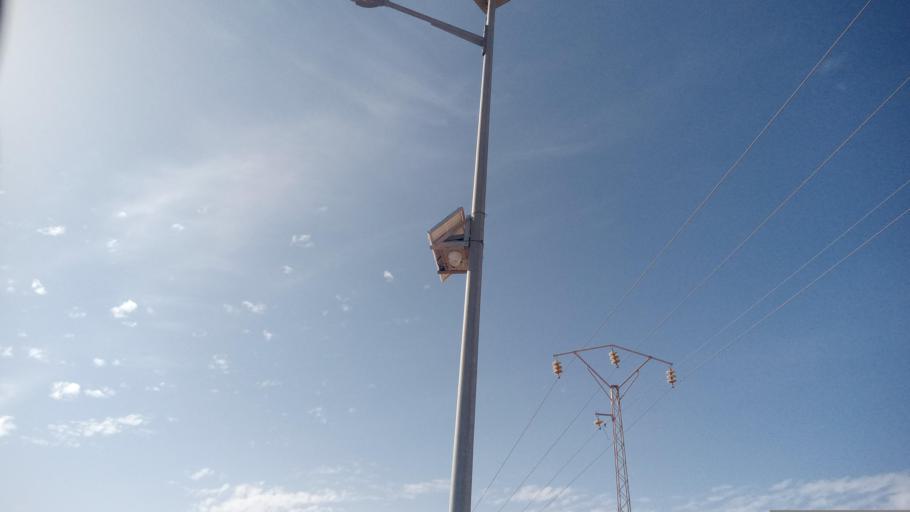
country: TN
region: Madanin
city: Zarzis
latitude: 33.4239
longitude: 10.8826
